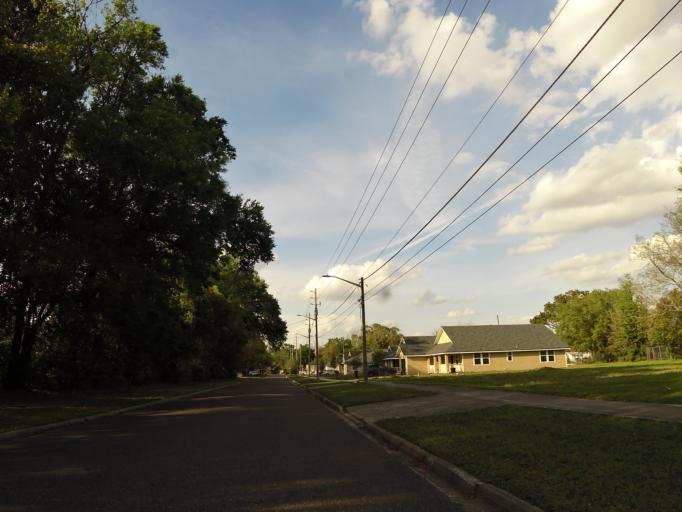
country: US
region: Florida
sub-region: Duval County
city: Jacksonville
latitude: 30.3492
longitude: -81.6716
